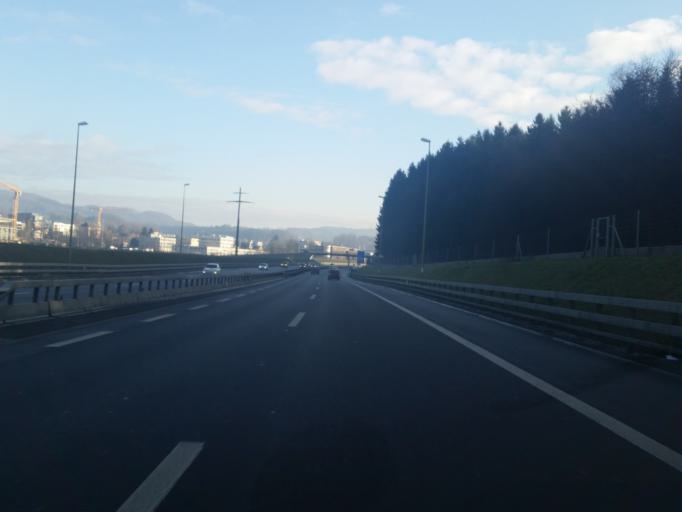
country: CH
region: Zurich
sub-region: Bezirk Affoltern
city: Obfelden / Toussen
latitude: 47.2766
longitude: 8.4316
